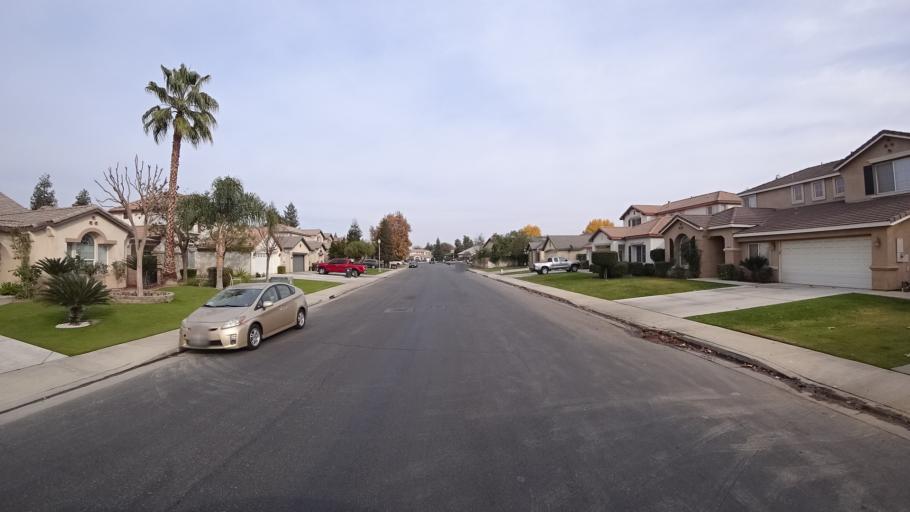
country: US
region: California
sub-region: Kern County
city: Rosedale
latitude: 35.3419
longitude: -119.1423
